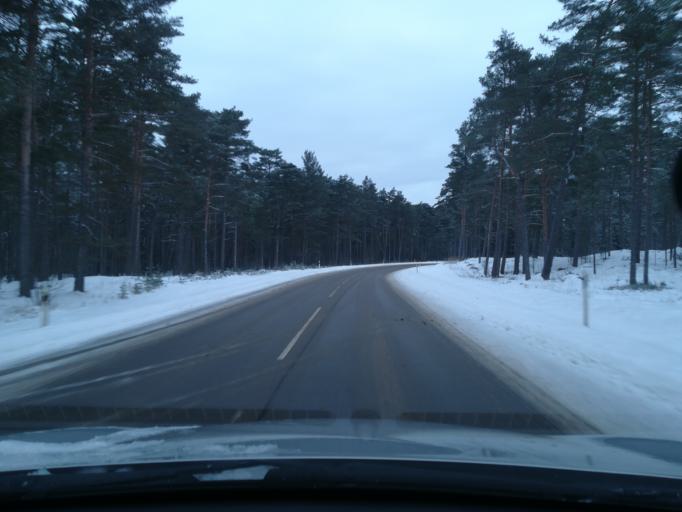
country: EE
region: Harju
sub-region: Keila linn
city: Keila
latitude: 59.4290
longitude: 24.3615
